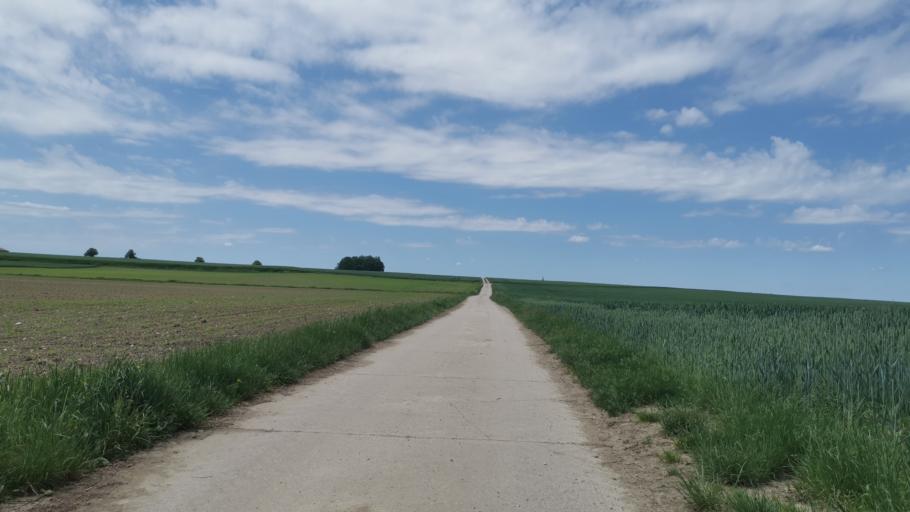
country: DE
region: Bavaria
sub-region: Swabia
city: Steindorf
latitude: 48.2394
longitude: 11.0132
